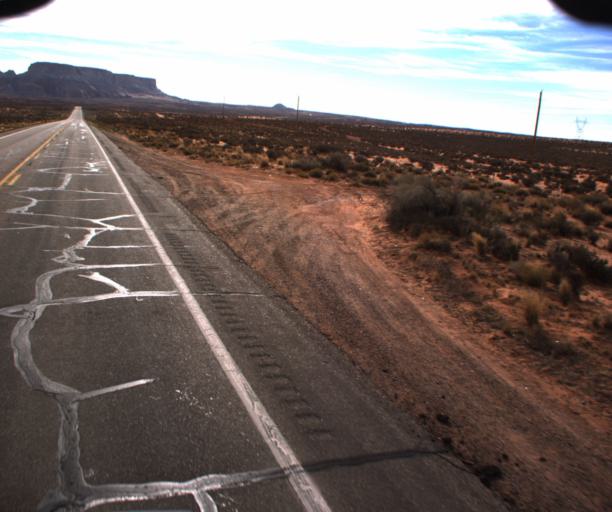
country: US
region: Arizona
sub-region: Coconino County
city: LeChee
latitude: 36.8851
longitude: -111.3582
